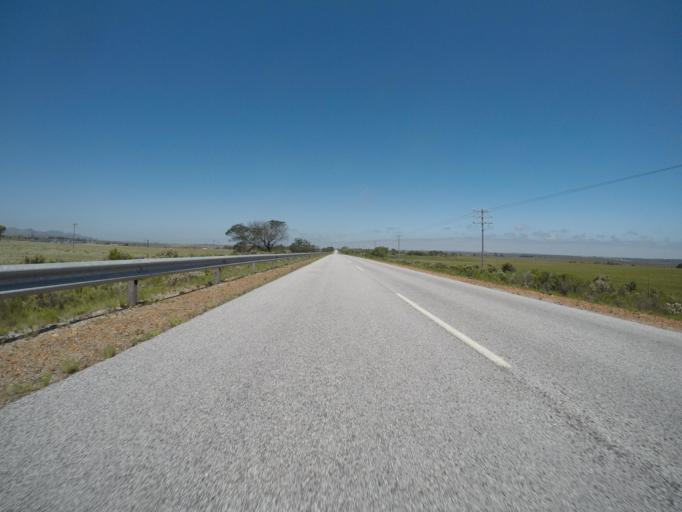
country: ZA
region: Eastern Cape
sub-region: Cacadu District Municipality
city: Kruisfontein
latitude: -34.0049
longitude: 24.5524
